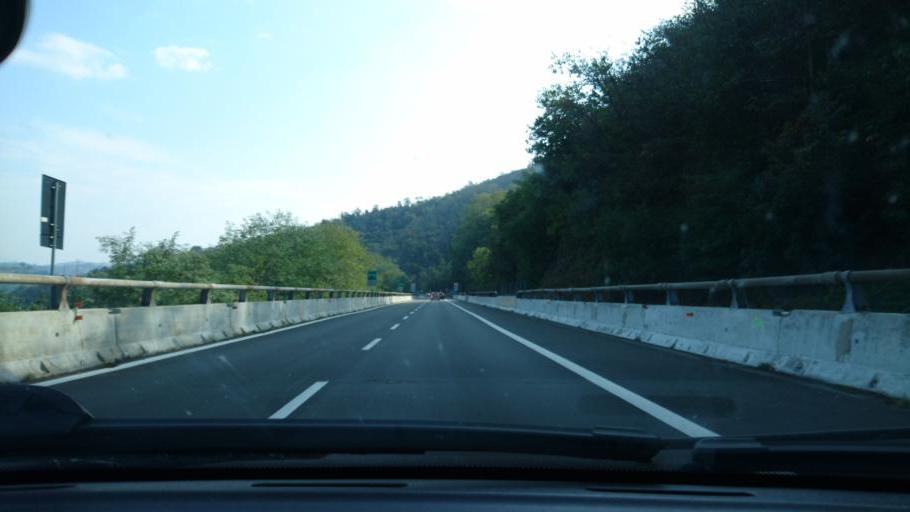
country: IT
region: Liguria
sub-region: Provincia di Savona
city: Altare
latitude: 44.3199
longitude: 8.3681
